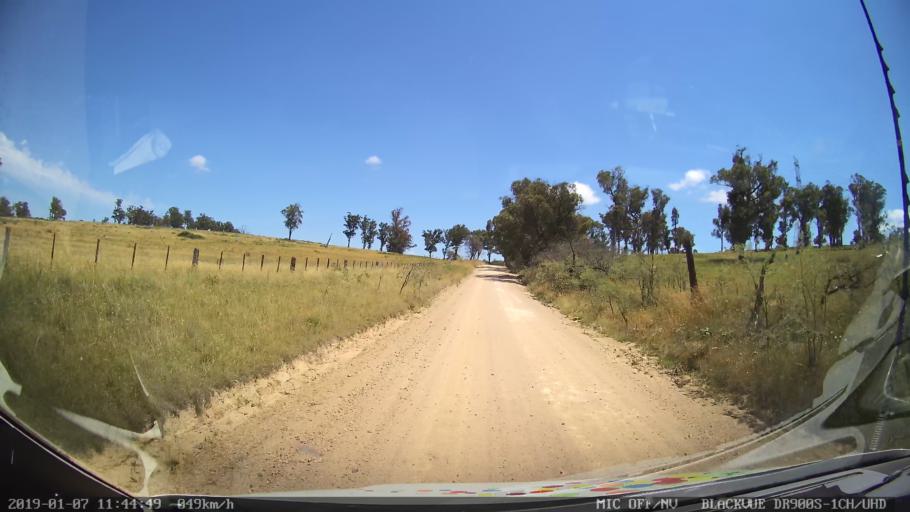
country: AU
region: New South Wales
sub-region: Guyra
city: Guyra
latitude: -30.3502
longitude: 151.6061
